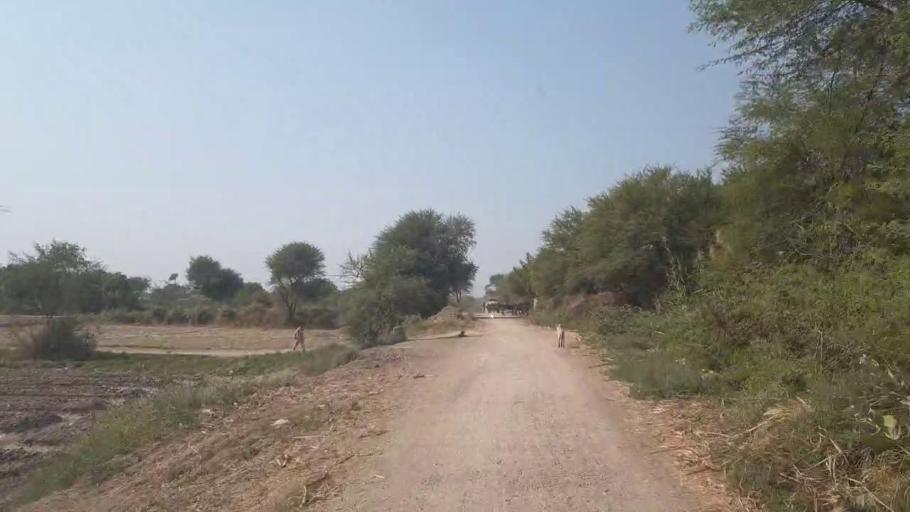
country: PK
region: Sindh
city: Tando Allahyar
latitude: 25.4794
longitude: 68.8023
